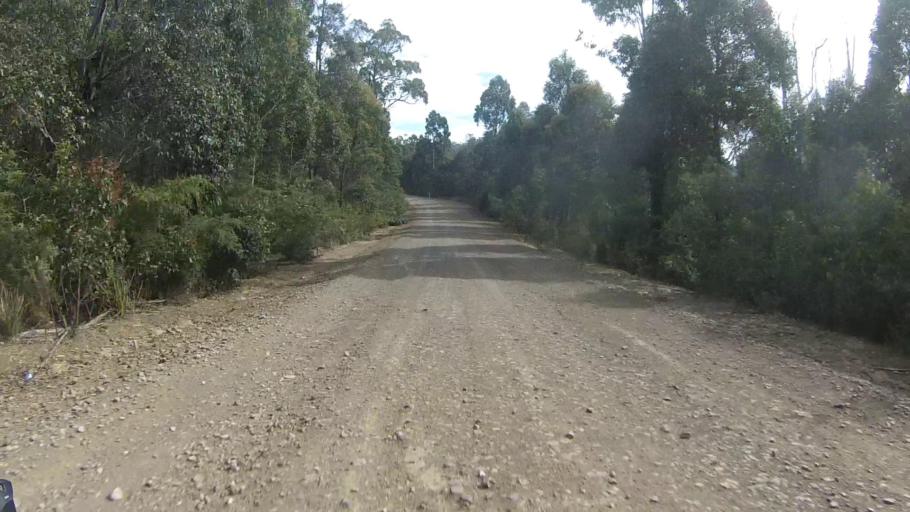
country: AU
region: Tasmania
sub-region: Sorell
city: Sorell
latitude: -42.7566
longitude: 147.8296
